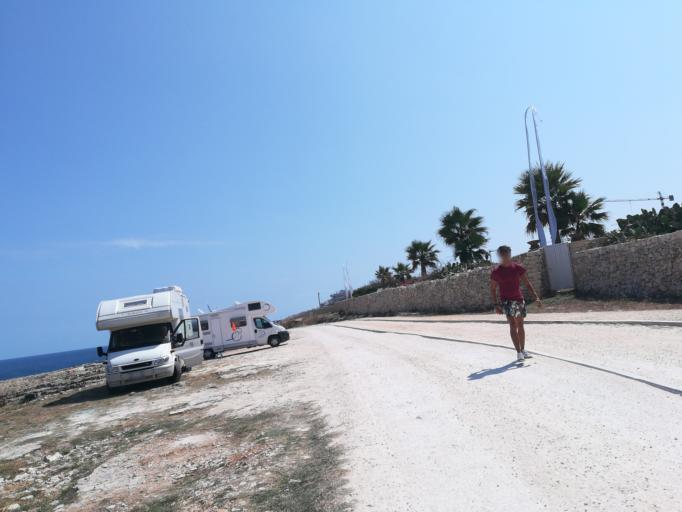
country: IT
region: Apulia
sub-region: Provincia di Bari
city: Polignano a Mare
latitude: 40.9996
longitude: 17.2106
